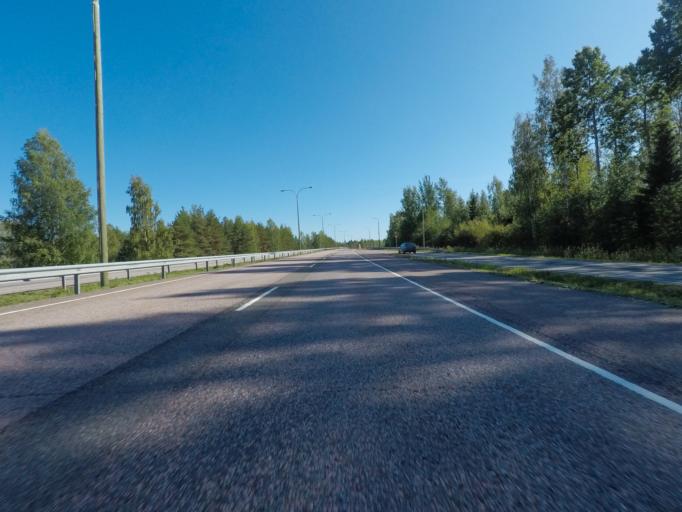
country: FI
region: Northern Savo
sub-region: Varkaus
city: Varkaus
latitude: 62.3168
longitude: 27.8483
